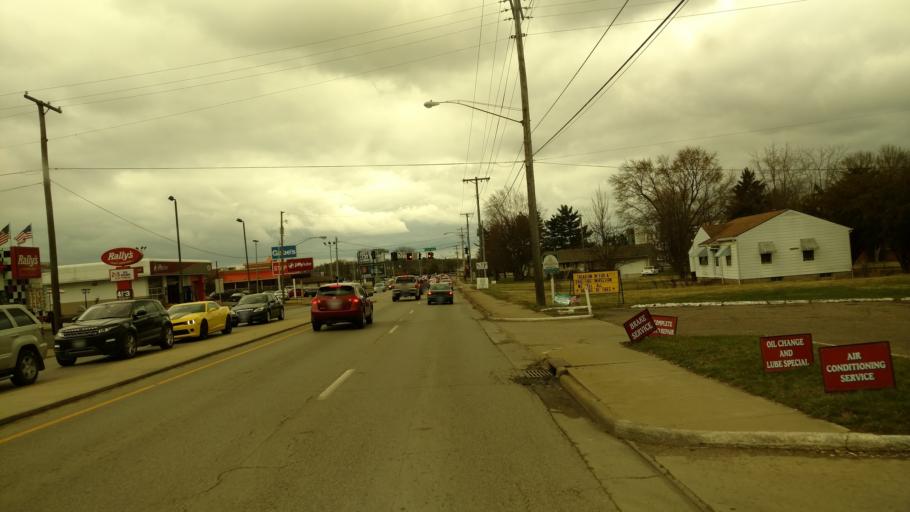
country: US
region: Ohio
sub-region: Muskingum County
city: North Zanesville
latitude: 39.9782
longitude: -82.0163
